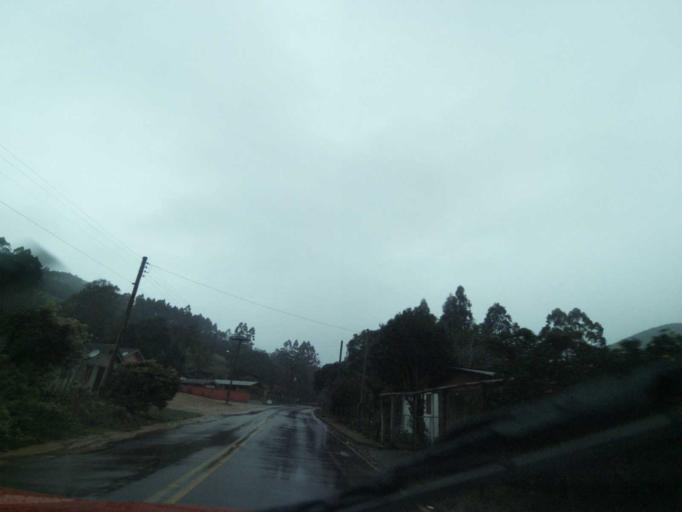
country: BR
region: Santa Catarina
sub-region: Anitapolis
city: Anitapolis
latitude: -27.8216
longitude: -49.0492
